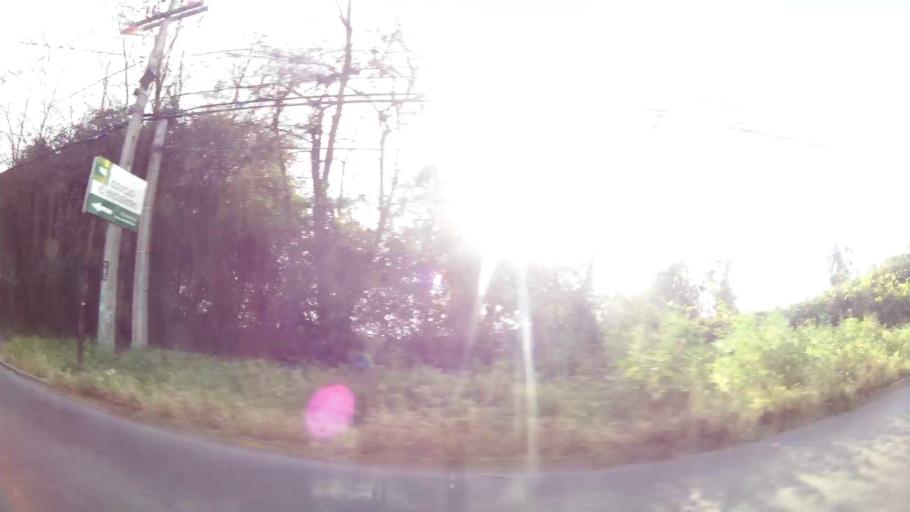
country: CL
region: Santiago Metropolitan
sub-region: Provincia de Santiago
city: Villa Presidente Frei, Nunoa, Santiago, Chile
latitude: -33.5022
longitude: -70.5527
